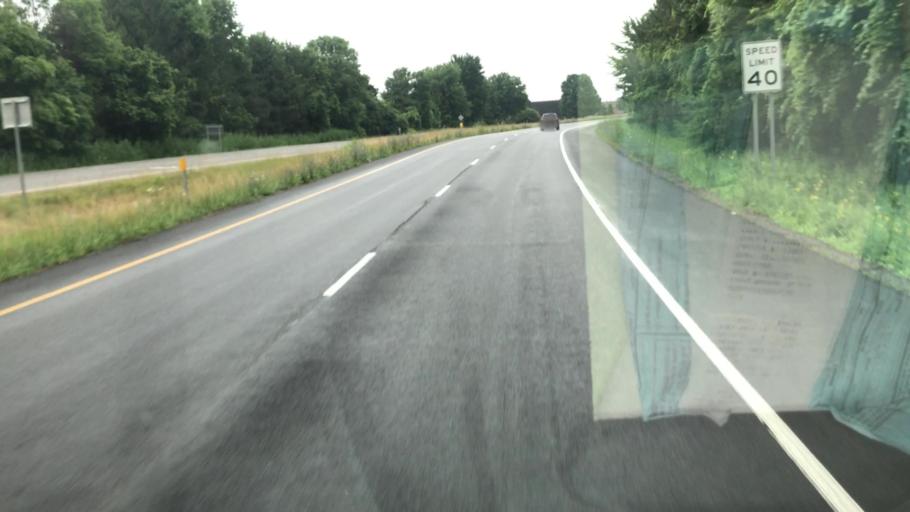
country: US
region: New York
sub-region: Onondaga County
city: Liverpool
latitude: 43.1405
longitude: -76.2090
